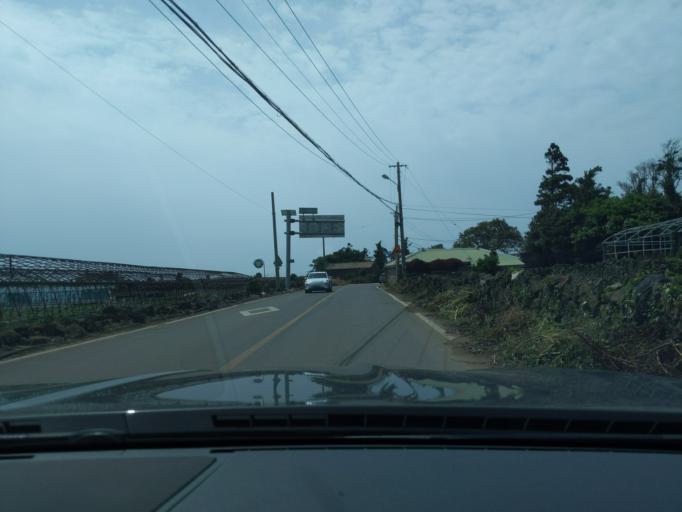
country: KR
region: Jeju-do
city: Gaigeturi
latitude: 33.2248
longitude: 126.2659
